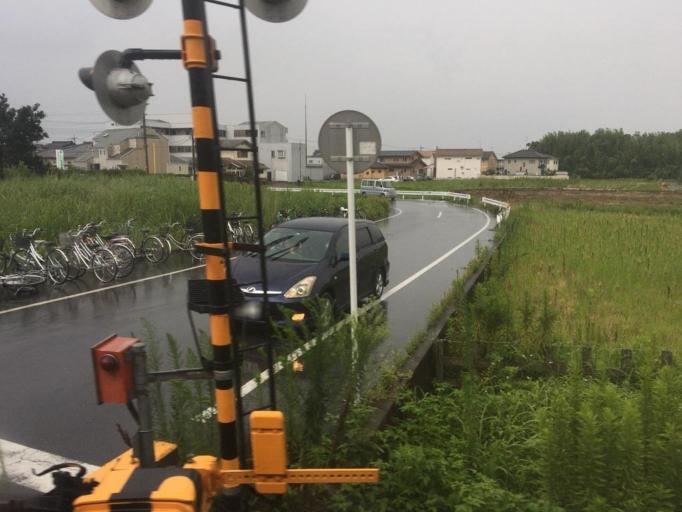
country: JP
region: Gunma
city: Ota
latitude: 36.2819
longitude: 139.3476
